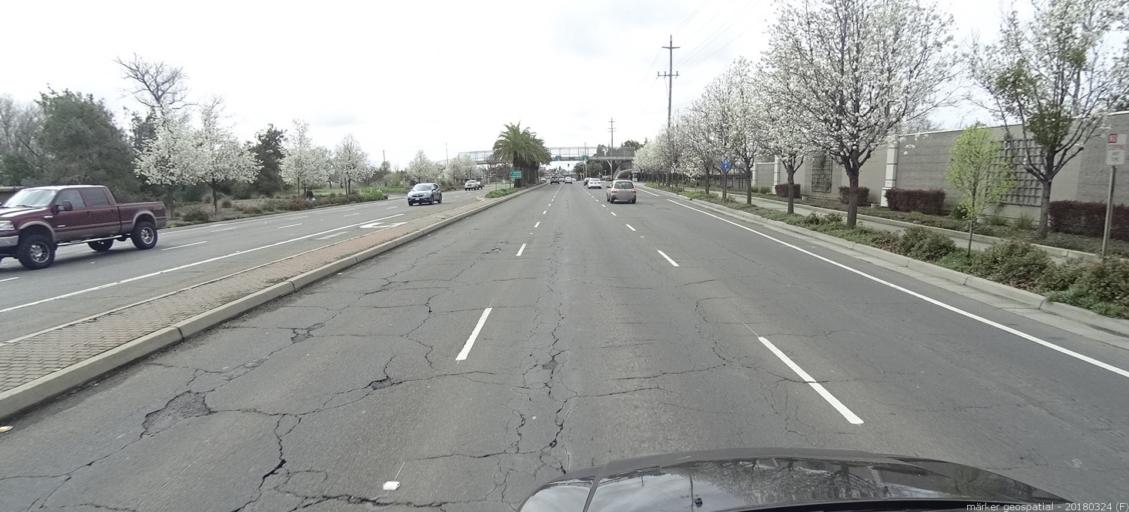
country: US
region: California
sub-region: Sacramento County
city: North Highlands
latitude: 38.6627
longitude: -121.3829
